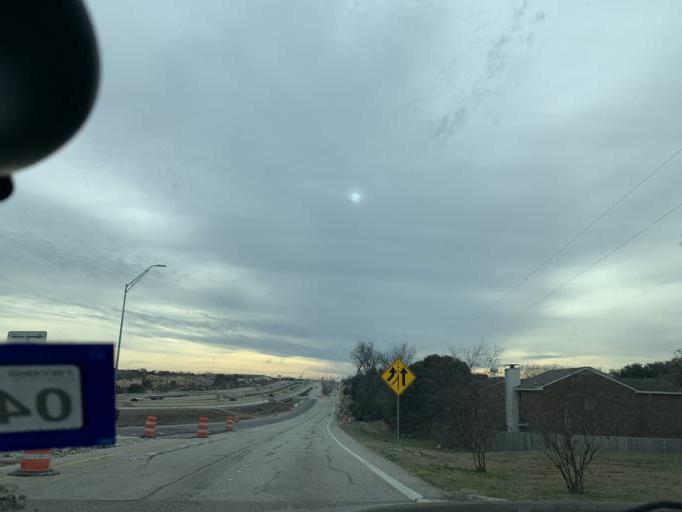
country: US
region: Texas
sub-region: Dallas County
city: Duncanville
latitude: 32.6310
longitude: -96.9029
